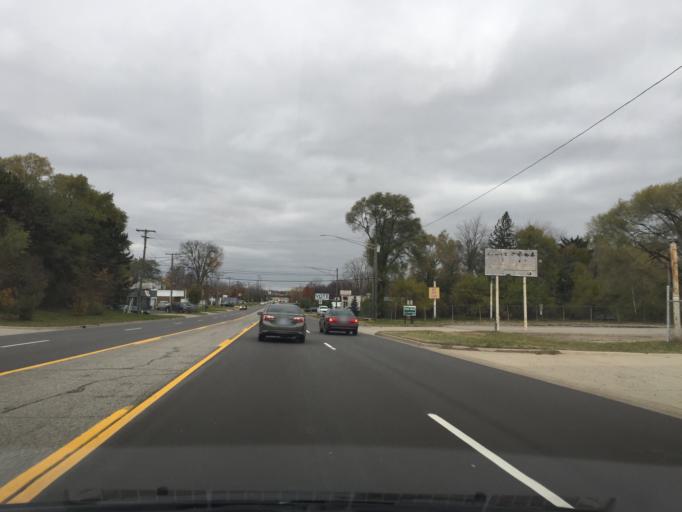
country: US
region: Michigan
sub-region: Oakland County
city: Pontiac
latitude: 42.6587
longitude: -83.3189
